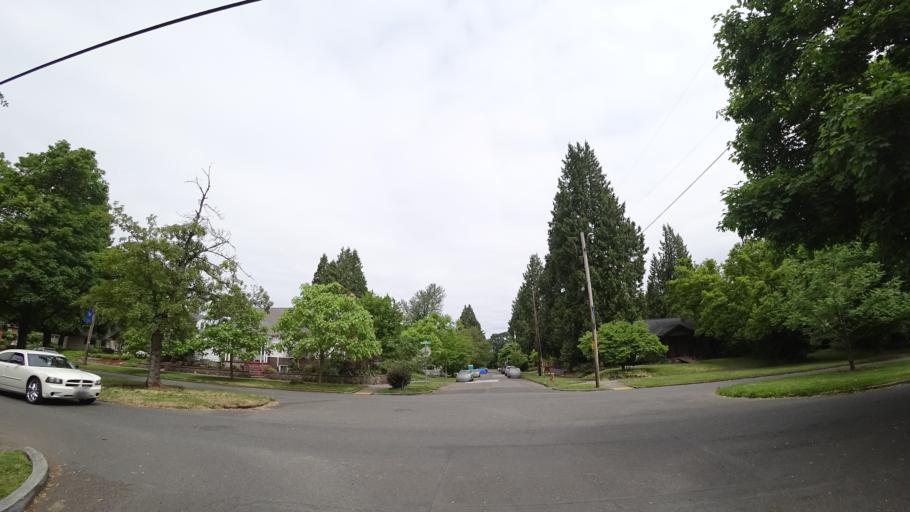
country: US
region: Oregon
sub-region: Multnomah County
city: Portland
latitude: 45.5662
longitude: -122.6371
